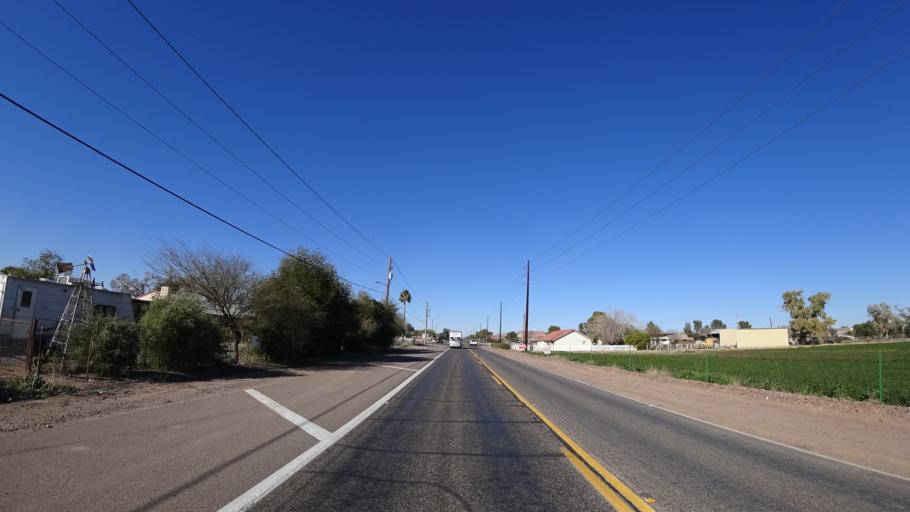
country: US
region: Arizona
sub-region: Maricopa County
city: Tolleson
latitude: 33.4200
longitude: -112.2896
